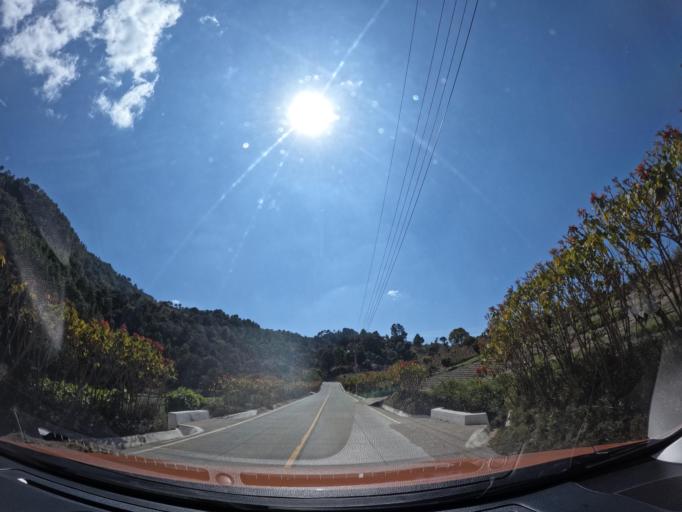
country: GT
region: Solola
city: San Antonio Palopo
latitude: 14.6965
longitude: -91.0702
